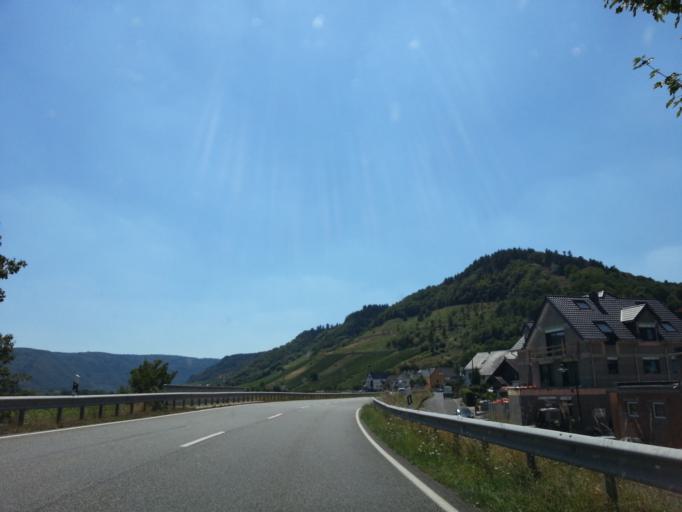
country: DE
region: Rheinland-Pfalz
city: Thornich
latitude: 49.8275
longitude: 6.8352
